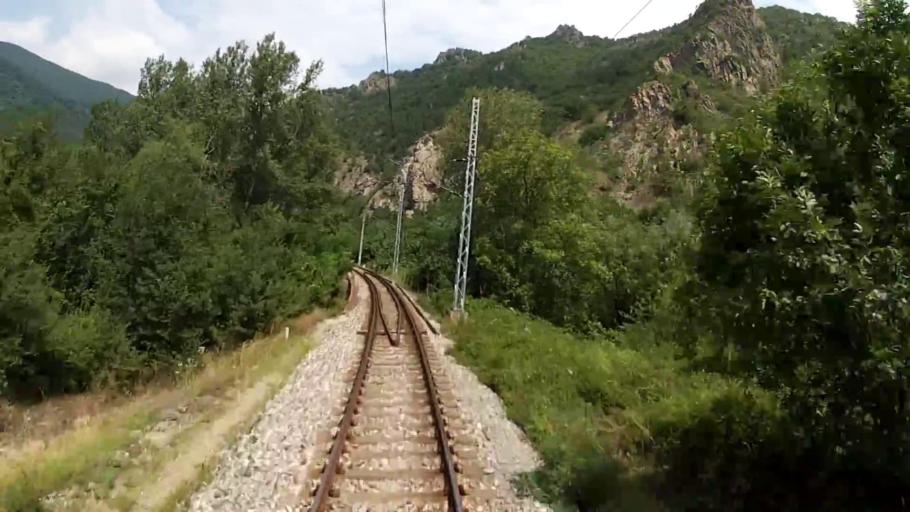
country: BG
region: Blagoevgrad
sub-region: Obshtina Kresna
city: Stara Kresna
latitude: 41.8120
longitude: 23.1633
